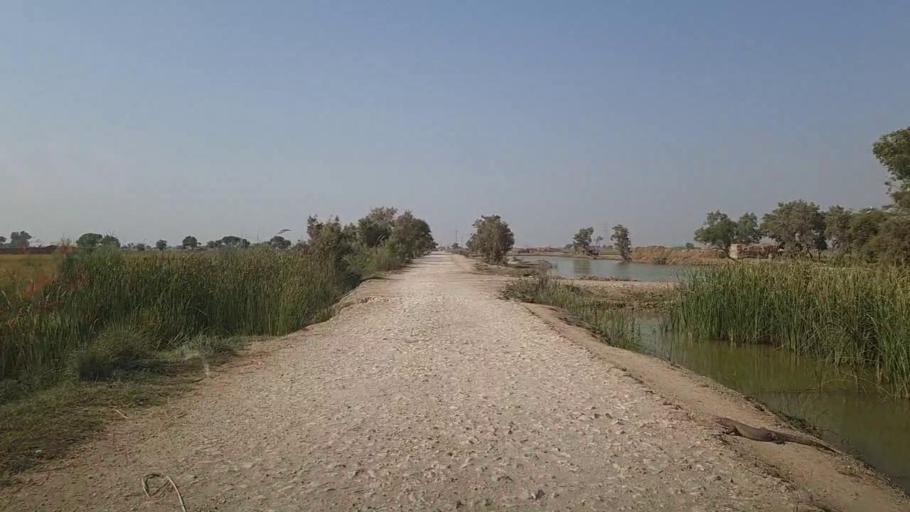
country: PK
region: Sindh
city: Kandhkot
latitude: 28.4047
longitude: 69.2559
